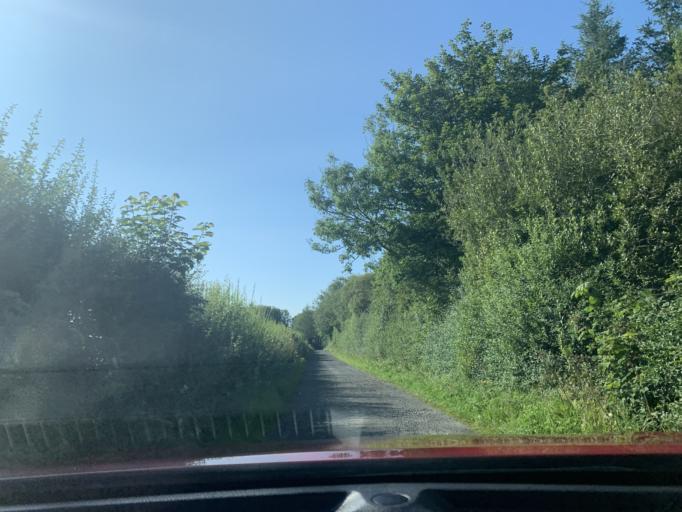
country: IE
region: Connaught
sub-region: Sligo
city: Tobercurry
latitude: 54.0606
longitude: -8.7938
